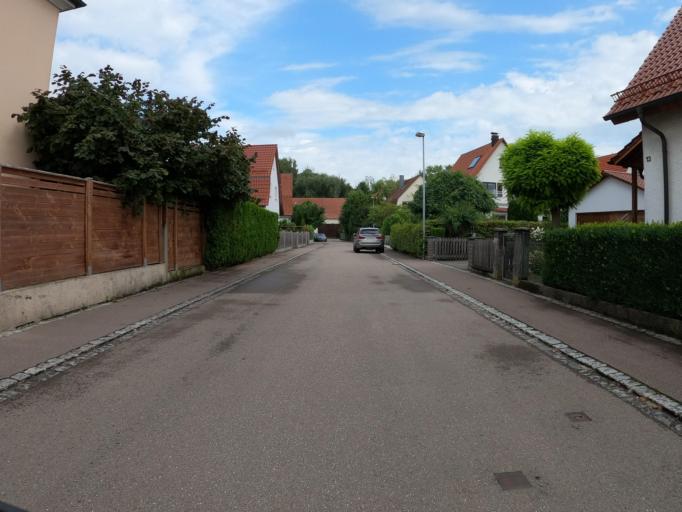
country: DE
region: Baden-Wuerttemberg
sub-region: Tuebingen Region
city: Langenau
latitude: 48.4974
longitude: 10.1251
